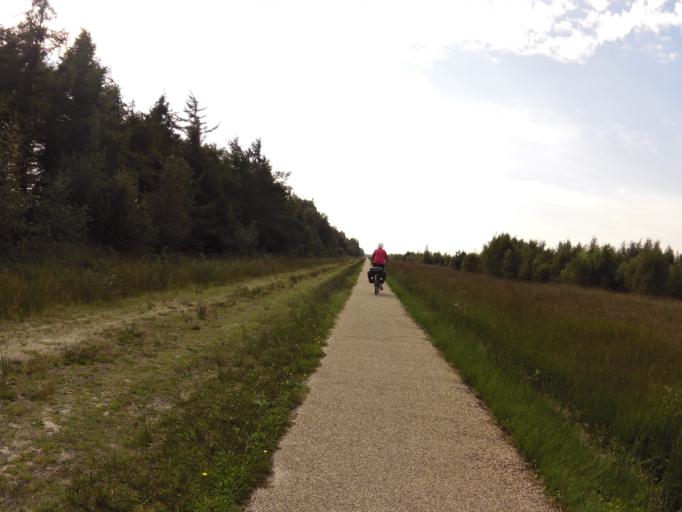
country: DE
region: Lower Saxony
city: Twist
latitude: 52.6747
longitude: 7.0583
